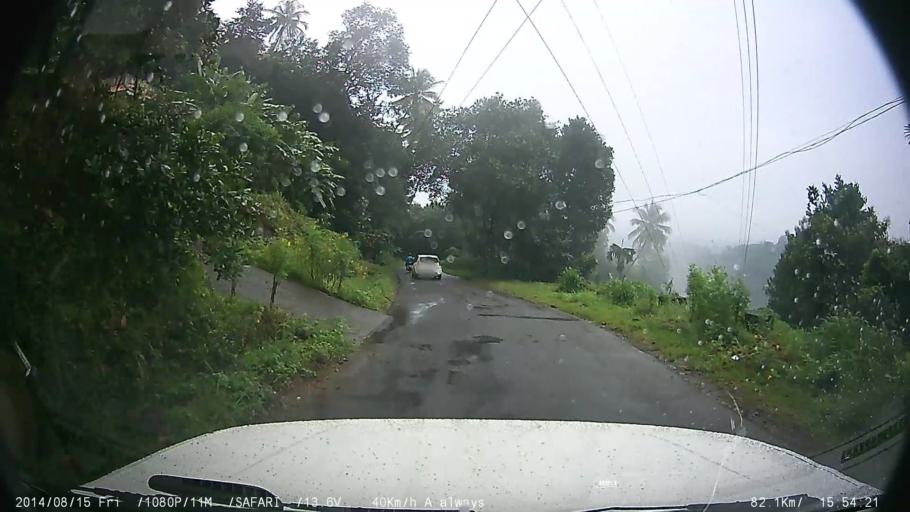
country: IN
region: Kerala
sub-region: Kottayam
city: Lalam
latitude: 9.7971
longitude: 76.7280
